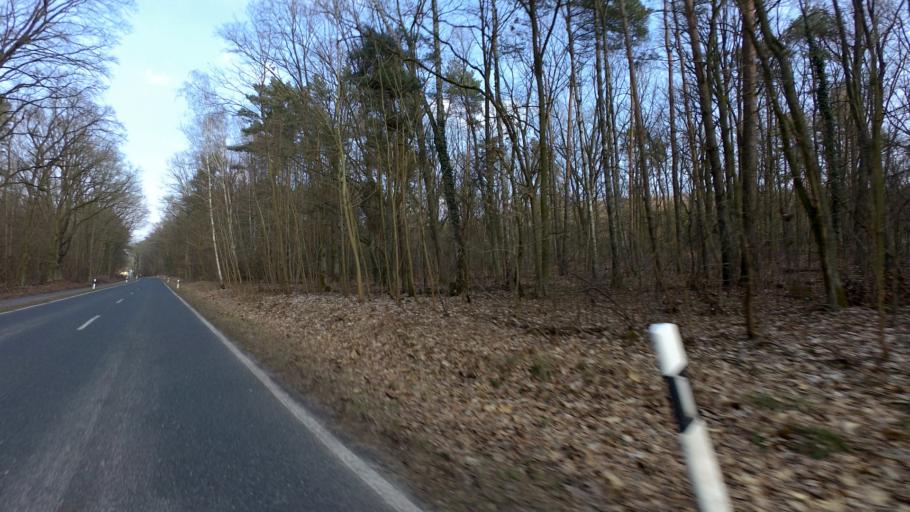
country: DE
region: Brandenburg
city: Werder
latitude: 52.3342
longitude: 12.9703
